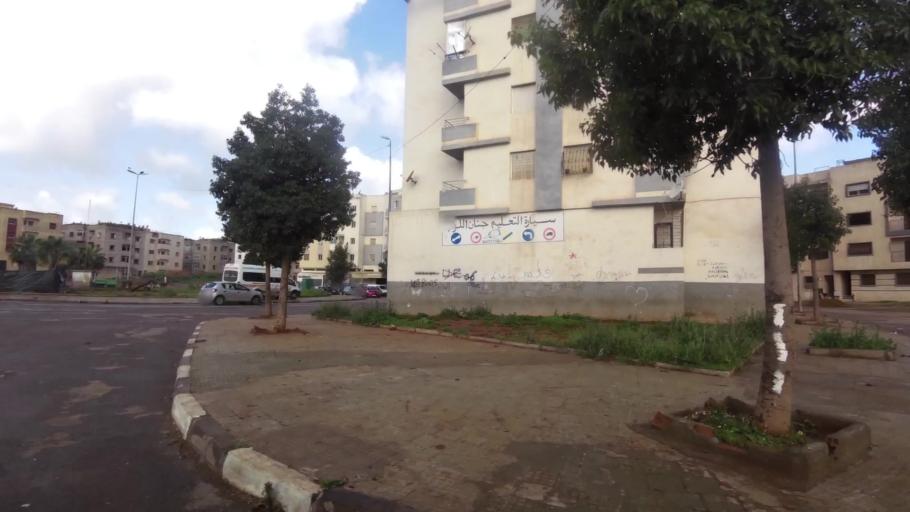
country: MA
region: Grand Casablanca
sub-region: Nouaceur
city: Bouskoura
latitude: 33.5360
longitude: -7.7015
